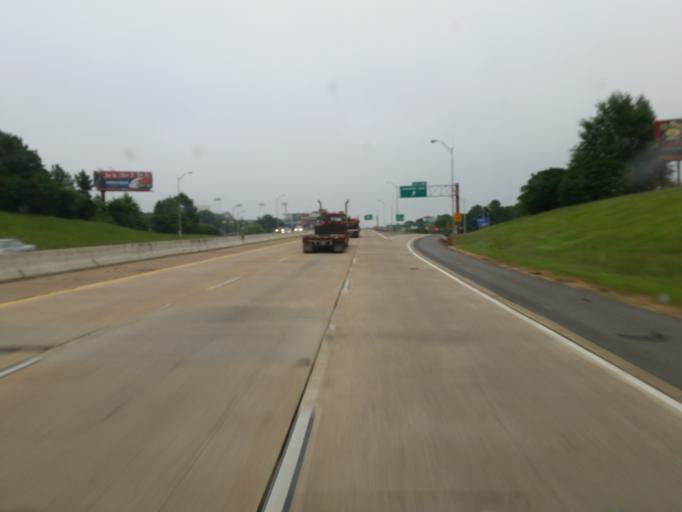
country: US
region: Louisiana
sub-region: Caddo Parish
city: Shreveport
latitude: 32.4709
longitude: -93.8012
